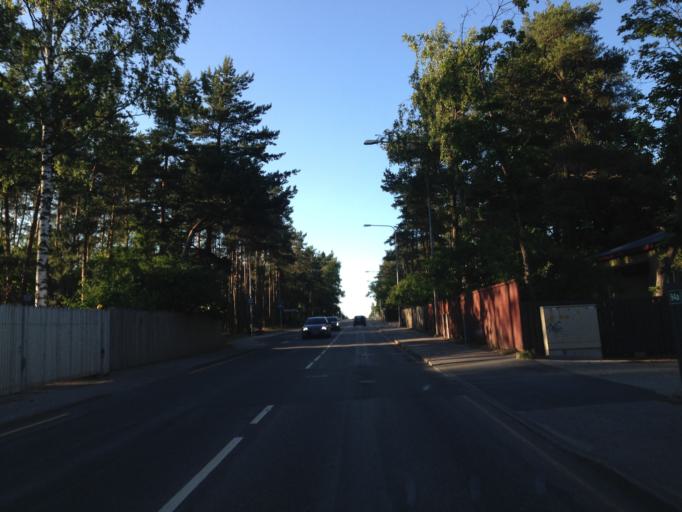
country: EE
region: Harju
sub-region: Saue vald
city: Laagri
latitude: 59.3817
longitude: 24.6379
